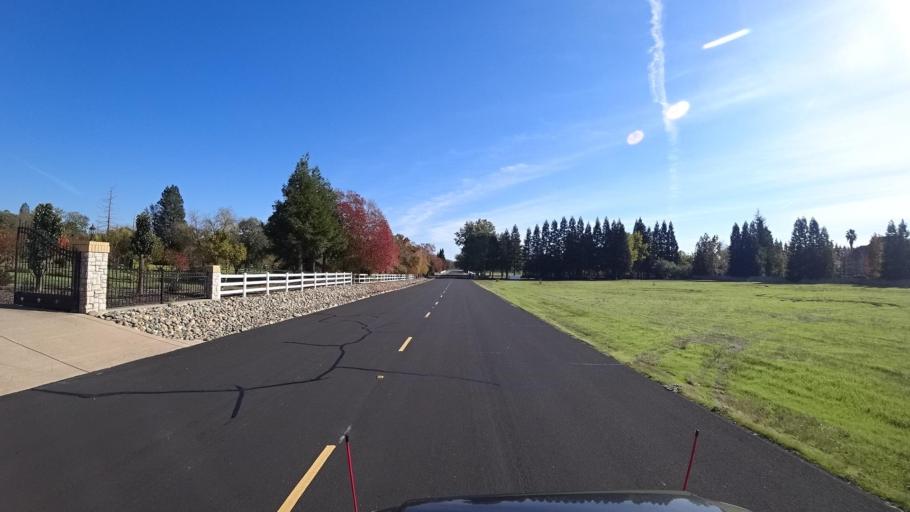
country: US
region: California
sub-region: Sacramento County
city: Wilton
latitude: 38.4334
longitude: -121.2794
